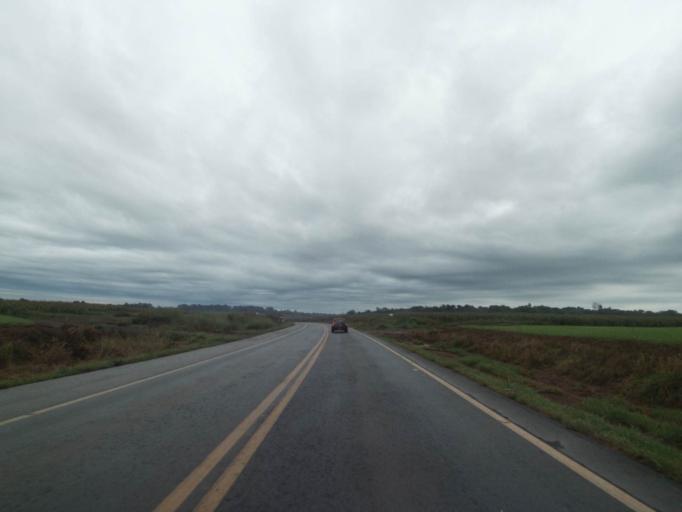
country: BR
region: Parana
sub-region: Toledo
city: Toledo
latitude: -24.6901
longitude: -53.7478
